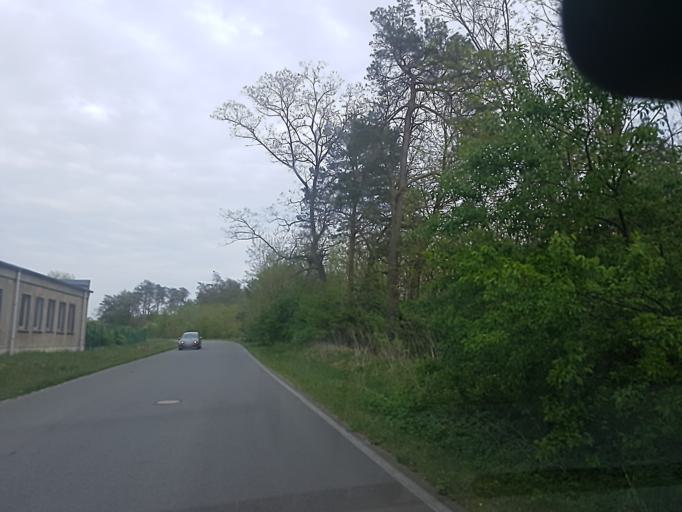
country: DE
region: Brandenburg
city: Finsterwalde
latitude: 51.6017
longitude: 13.7420
